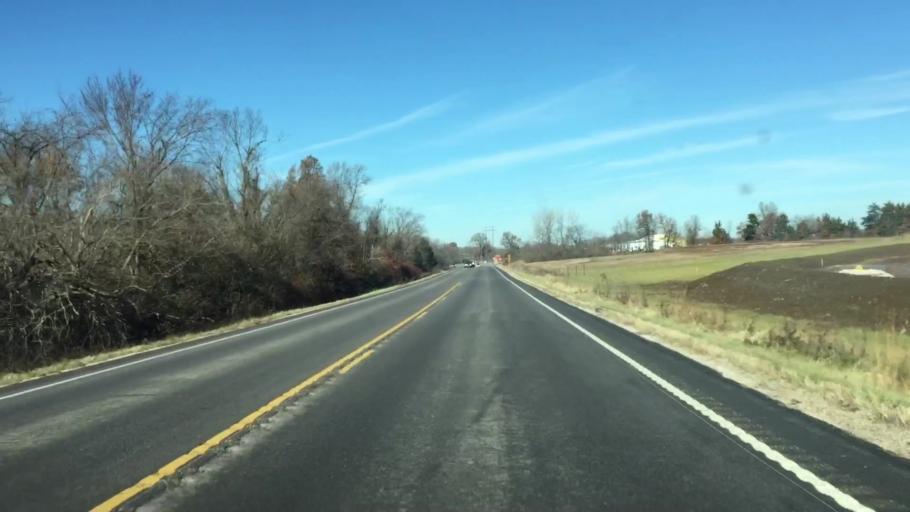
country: US
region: Missouri
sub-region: Miller County
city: Eldon
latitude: 38.3588
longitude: -92.6030
